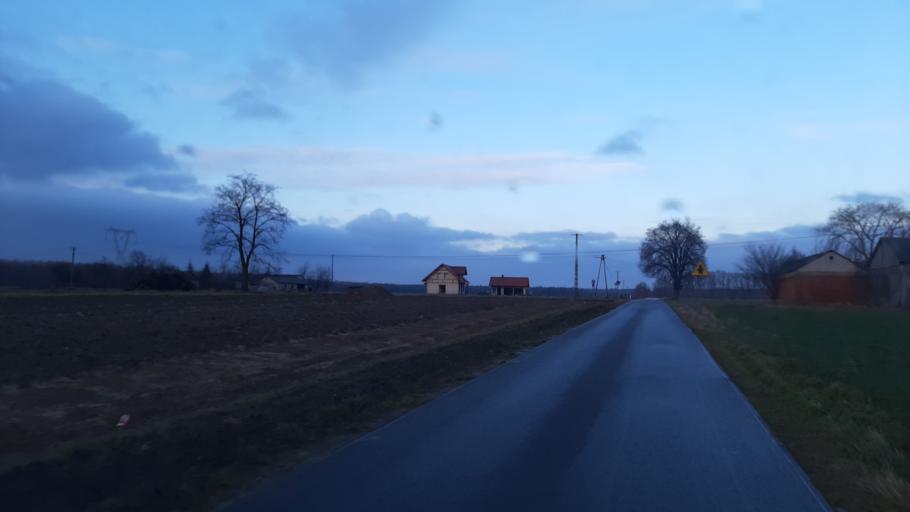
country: PL
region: Lublin Voivodeship
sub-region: Powiat lubelski
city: Garbow
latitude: 51.3637
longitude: 22.3974
